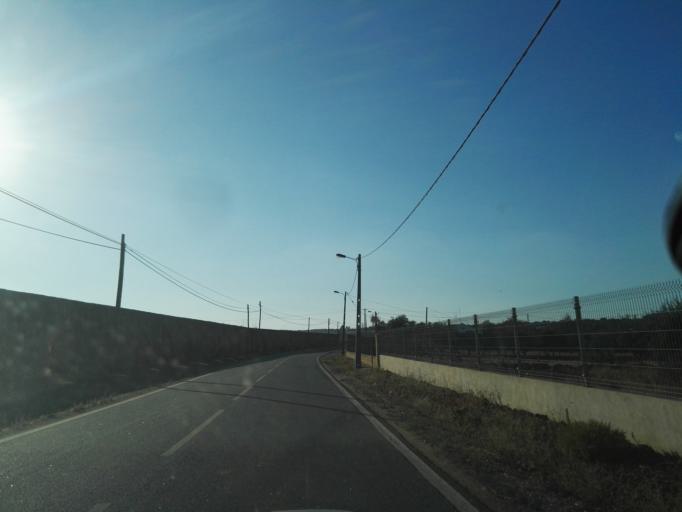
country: PT
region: Portalegre
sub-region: Elvas
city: Elvas
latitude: 38.8789
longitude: -7.1871
